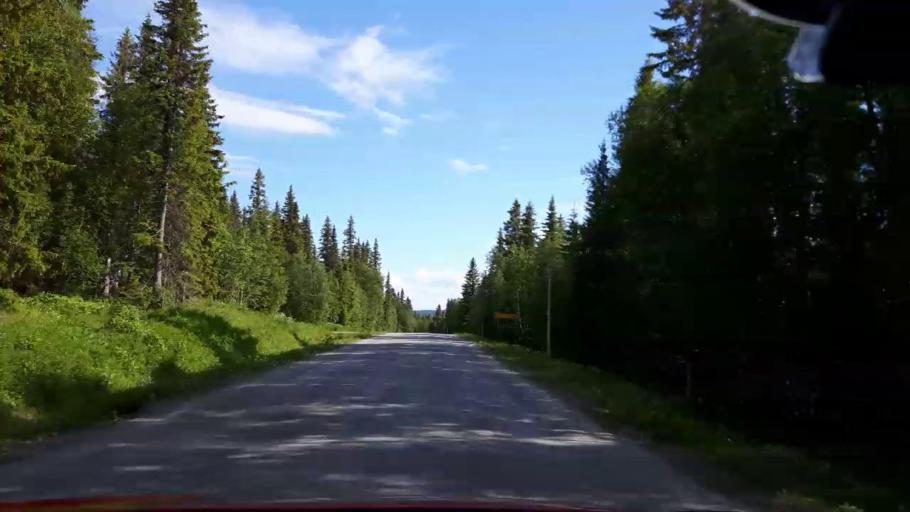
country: SE
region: Jaemtland
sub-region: Krokoms Kommun
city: Valla
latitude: 63.7753
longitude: 14.0453
